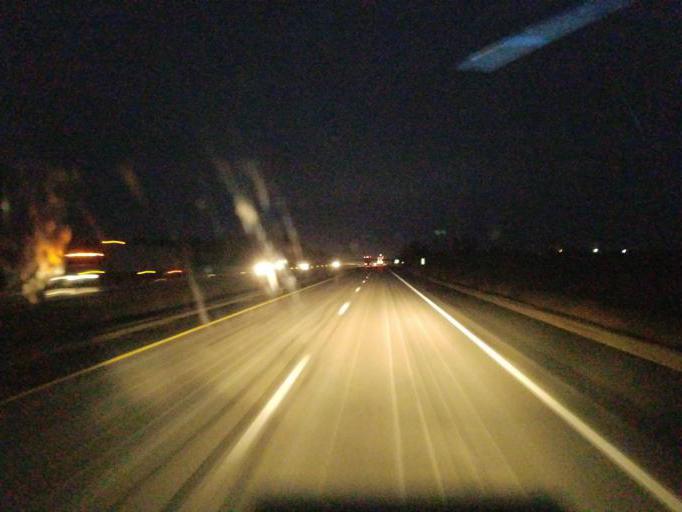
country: US
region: Iowa
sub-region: Guthrie County
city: Stuart
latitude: 41.4958
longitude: -94.4203
